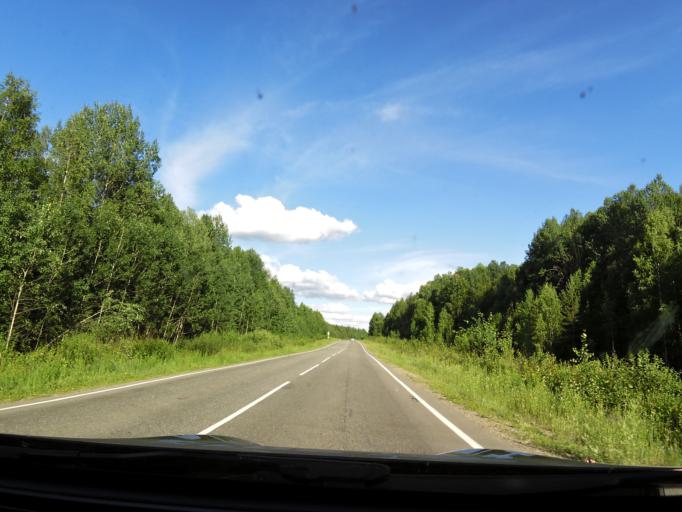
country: RU
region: Kirov
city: Omutninsk
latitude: 58.7555
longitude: 52.0375
